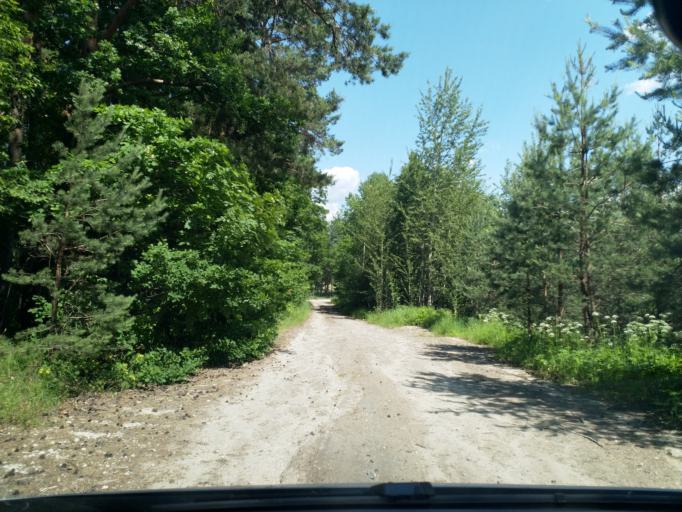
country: LV
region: Kuldigas Rajons
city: Kuldiga
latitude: 56.9695
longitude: 21.9260
